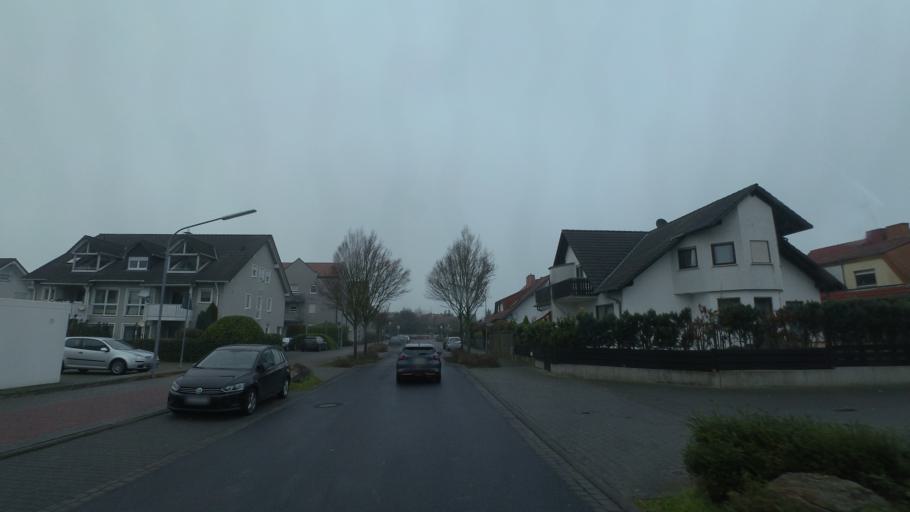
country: DE
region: Hesse
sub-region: Regierungsbezirk Darmstadt
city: Seligenstadt
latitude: 50.0422
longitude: 8.9600
